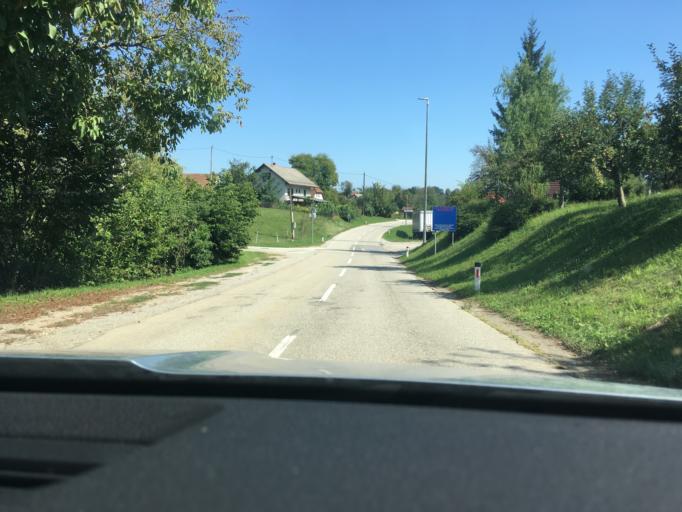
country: SI
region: Metlika
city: Metlika
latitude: 45.5213
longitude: 15.3131
